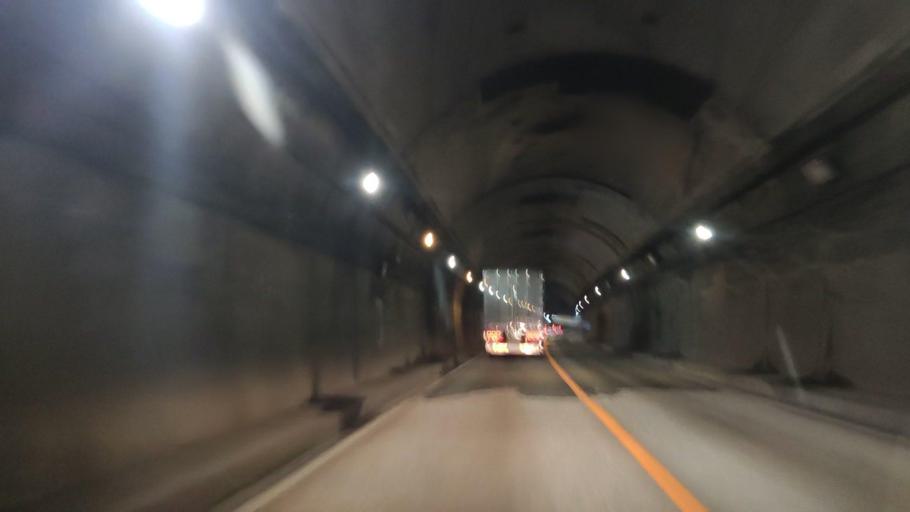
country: JP
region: Aomori
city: Aomori Shi
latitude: 40.7730
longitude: 140.9815
